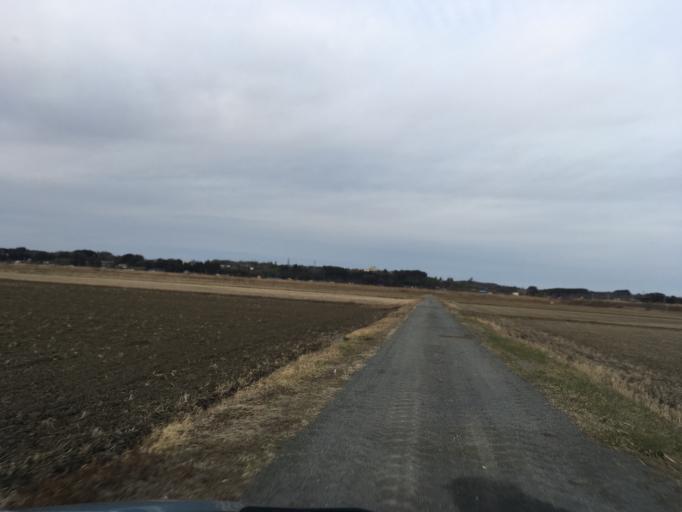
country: JP
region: Miyagi
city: Kogota
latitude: 38.6407
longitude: 141.0673
